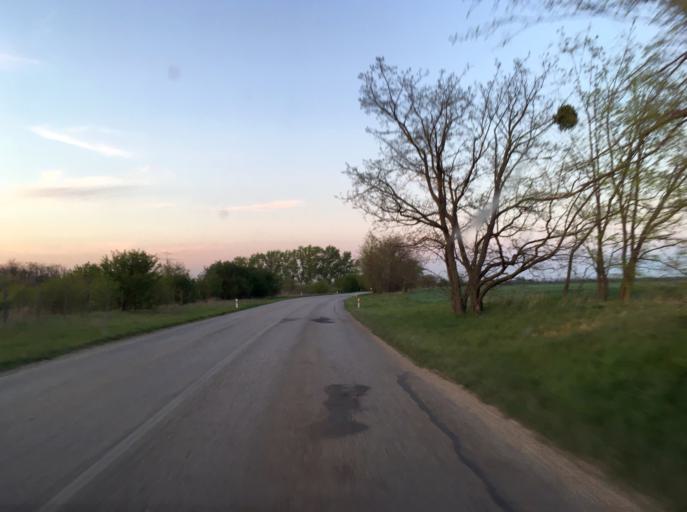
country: SK
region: Nitriansky
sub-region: Okres Nove Zamky
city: Nove Zamky
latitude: 47.9397
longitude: 18.1283
